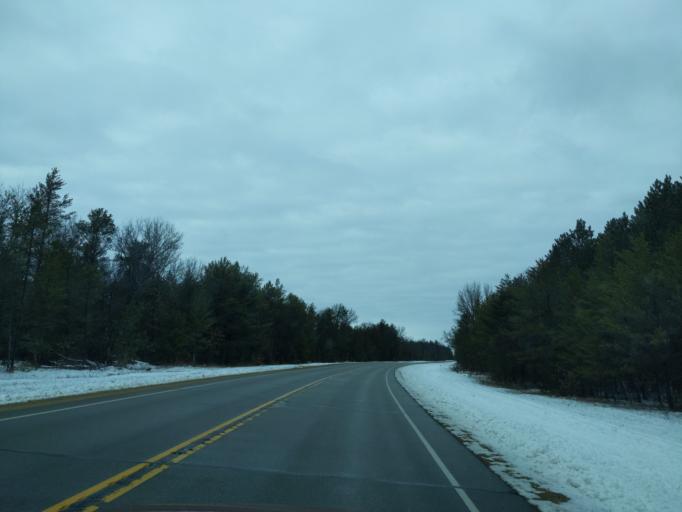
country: US
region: Wisconsin
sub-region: Waushara County
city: Wautoma
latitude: 43.9675
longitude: -89.3273
